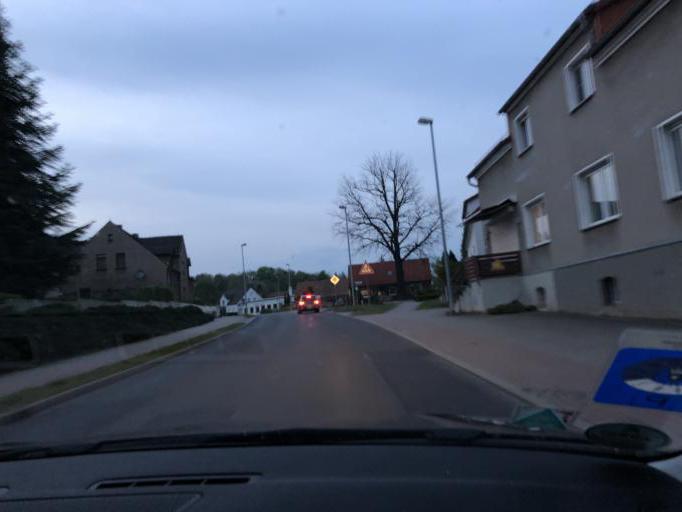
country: DE
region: Saxony
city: Krauschwitz
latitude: 51.5183
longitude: 14.7157
